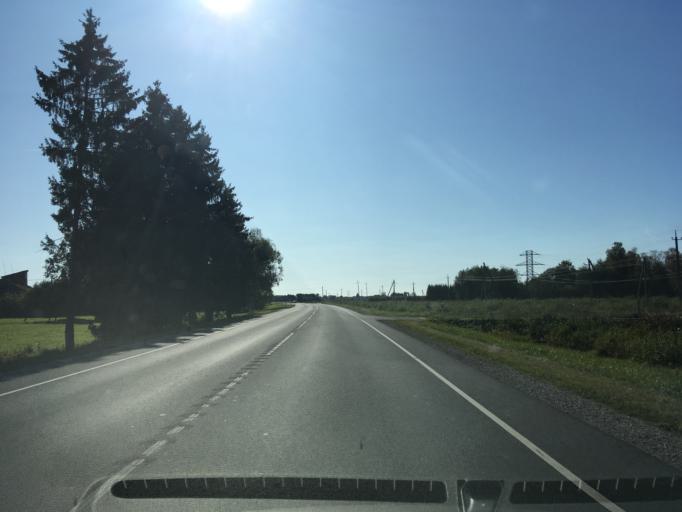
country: EE
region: Harju
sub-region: Nissi vald
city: Turba
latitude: 58.8861
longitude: 24.0903
